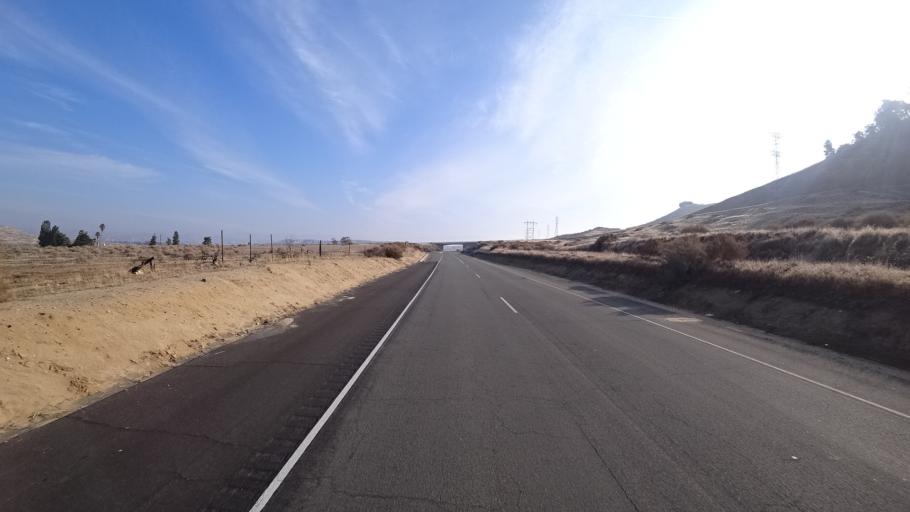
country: US
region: California
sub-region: Kern County
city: Oildale
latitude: 35.4167
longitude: -118.9623
